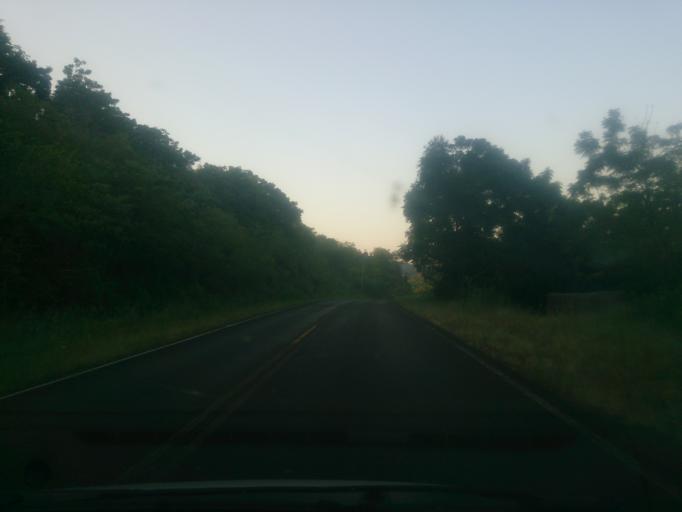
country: AR
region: Misiones
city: Panambi
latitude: -27.6822
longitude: -54.9079
